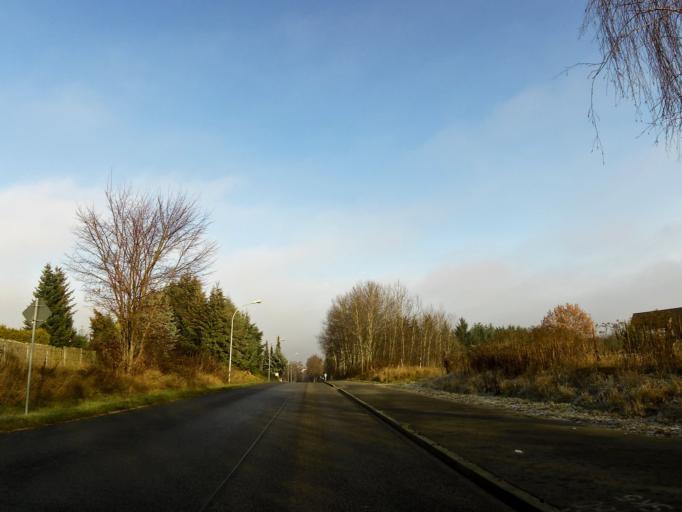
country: DE
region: Brandenburg
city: Werder
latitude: 52.3518
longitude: 12.9055
